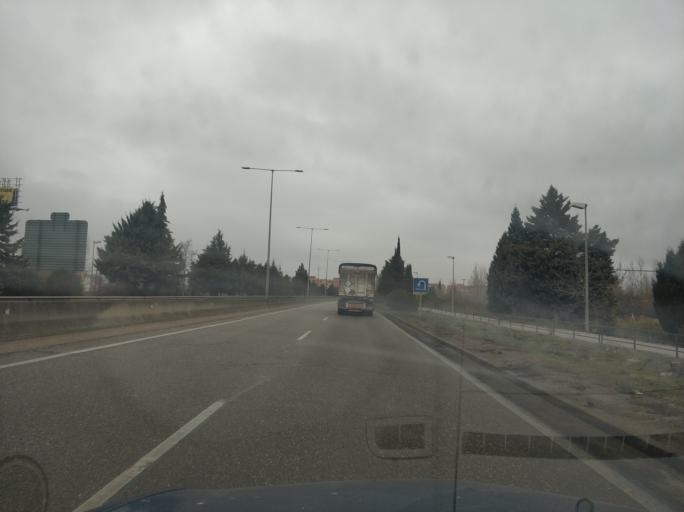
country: ES
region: Castille and Leon
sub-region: Provincia de Valladolid
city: Valladolid
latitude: 41.6379
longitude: -4.7024
